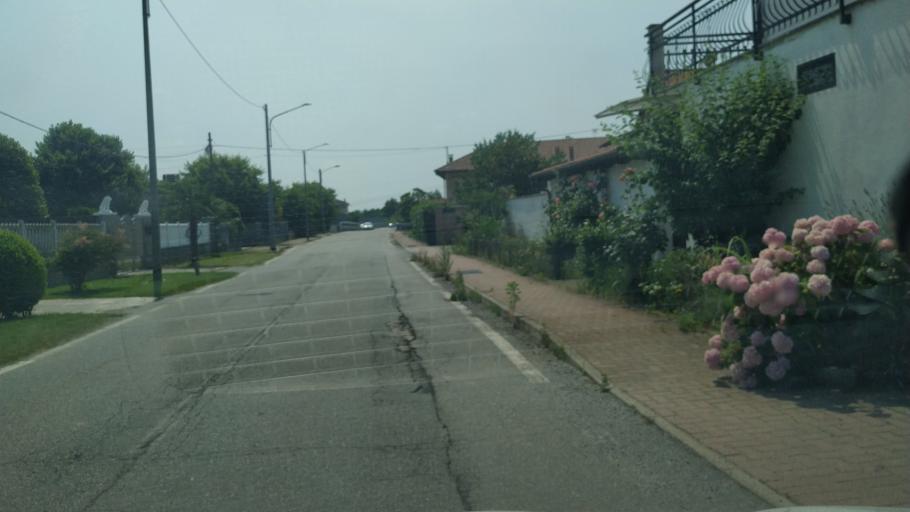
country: IT
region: Piedmont
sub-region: Provincia di Torino
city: Rondissone
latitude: 45.2428
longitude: 7.9704
